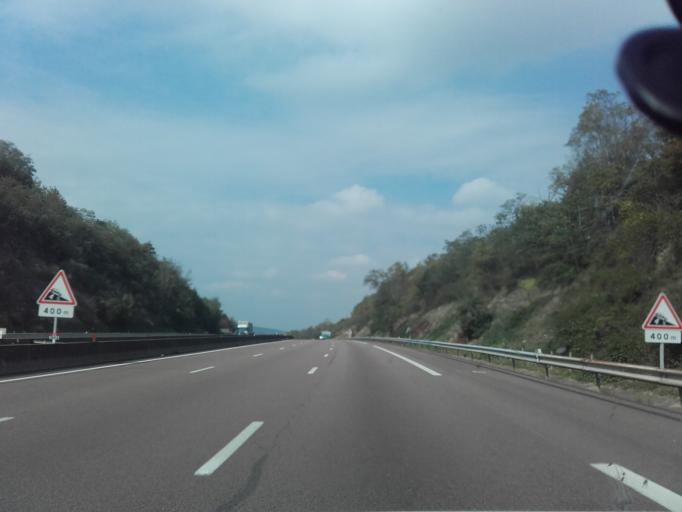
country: FR
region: Bourgogne
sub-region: Departement de Saone-et-Loire
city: Tournus
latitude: 46.5893
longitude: 4.8994
